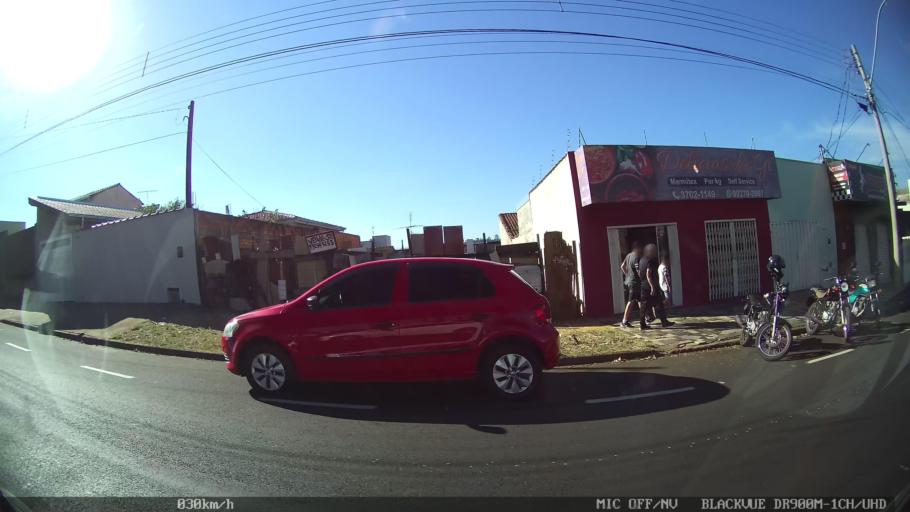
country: BR
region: Sao Paulo
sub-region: Franca
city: Franca
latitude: -20.4893
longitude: -47.4091
